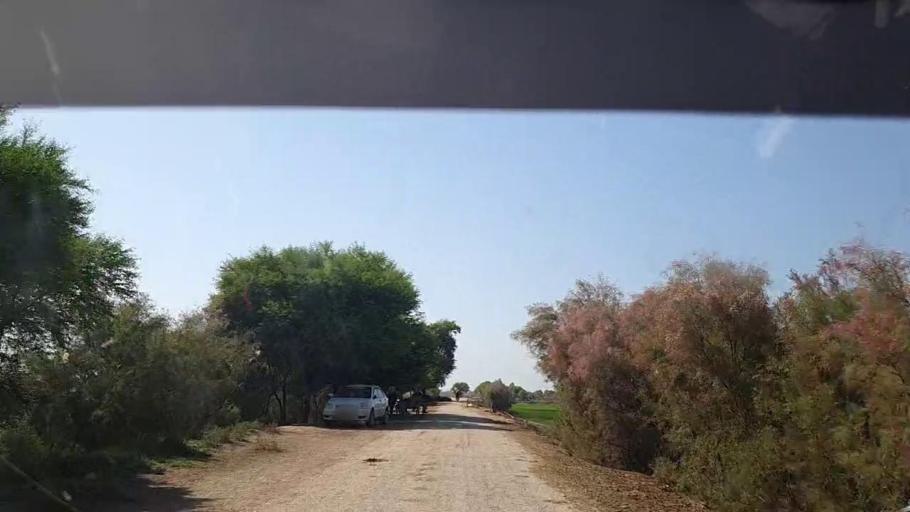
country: PK
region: Sindh
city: Ghauspur
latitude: 28.1944
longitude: 69.0510
